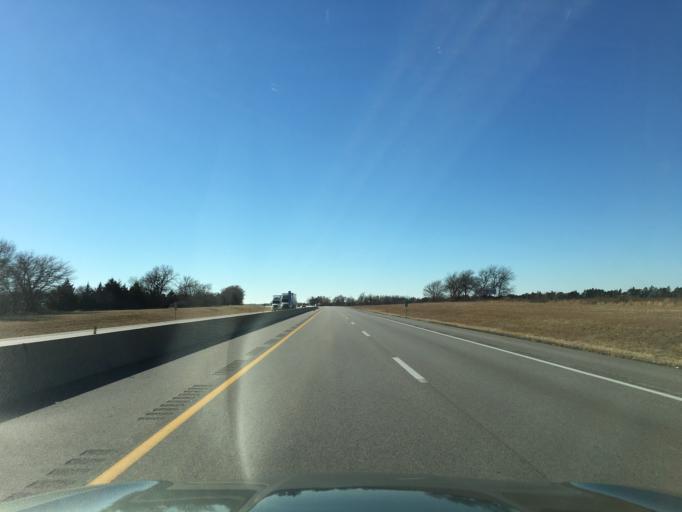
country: US
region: Kansas
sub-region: Sumner County
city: Wellington
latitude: 37.3313
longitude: -97.3345
